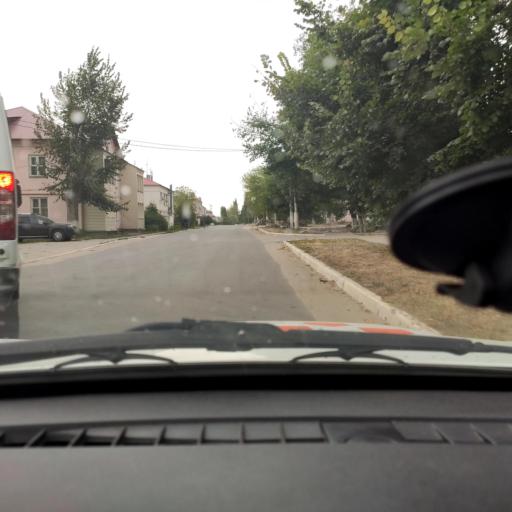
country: RU
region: Voronezj
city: Strelitsa
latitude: 51.6125
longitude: 38.9013
